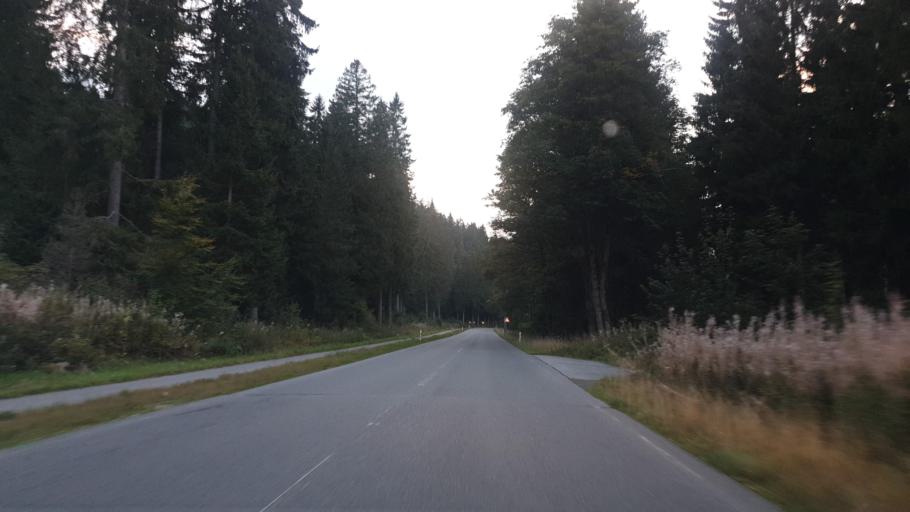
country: DE
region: Saxony
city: Sosa
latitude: 50.4384
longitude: 12.6407
